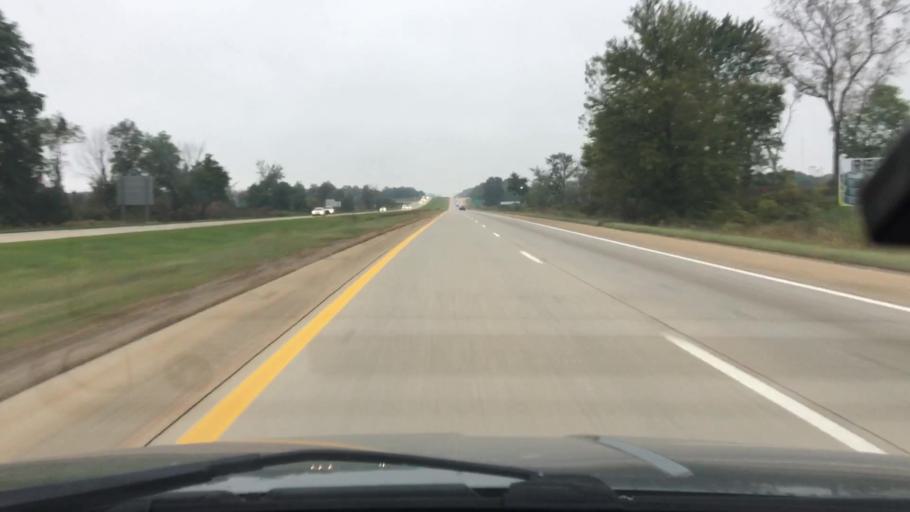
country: US
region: Michigan
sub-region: Jackson County
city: Concord
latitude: 42.2624
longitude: -84.6342
